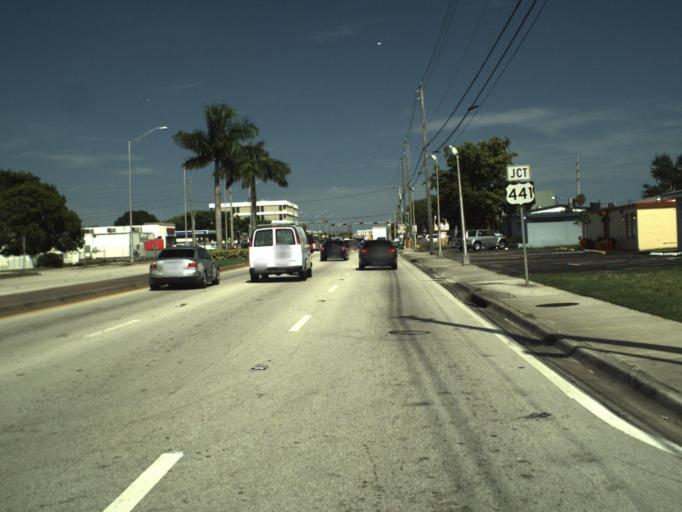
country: US
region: Florida
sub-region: Miami-Dade County
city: Norland
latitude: 25.9423
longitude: -80.2076
